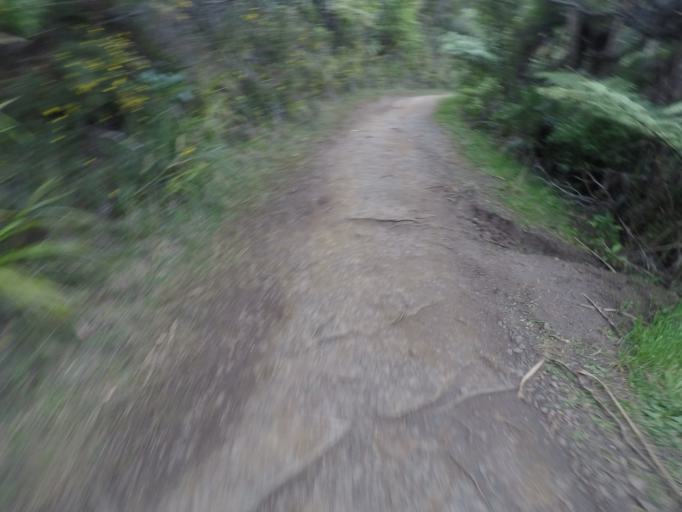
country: NZ
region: Auckland
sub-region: Auckland
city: Muriwai Beach
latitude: -36.9722
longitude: 174.4680
